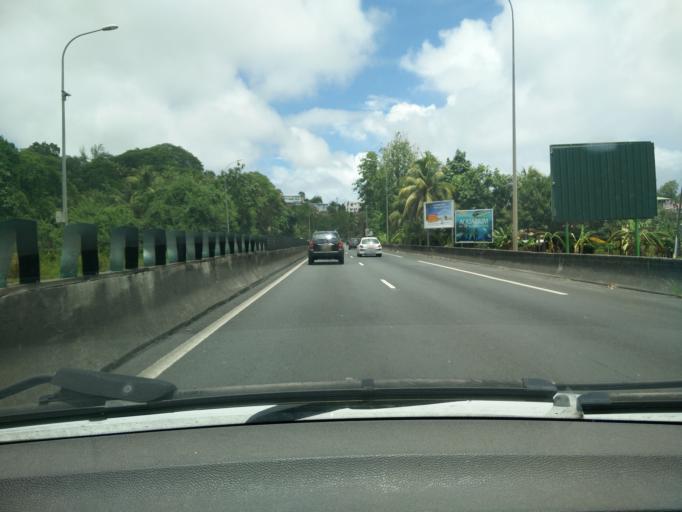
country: GP
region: Guadeloupe
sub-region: Guadeloupe
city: Pointe-a-Pitre
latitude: 16.2446
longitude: -61.5241
